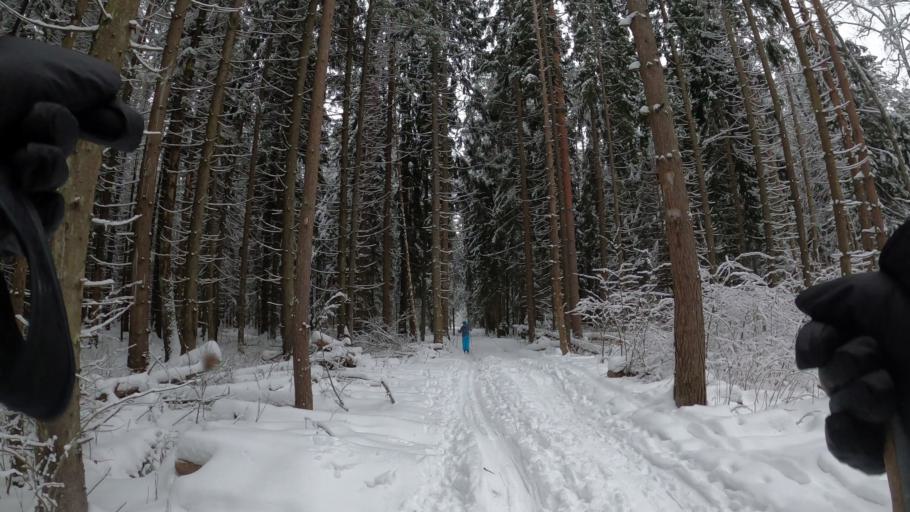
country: RU
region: Moskovskaya
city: Firsanovka
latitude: 55.9584
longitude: 37.2224
